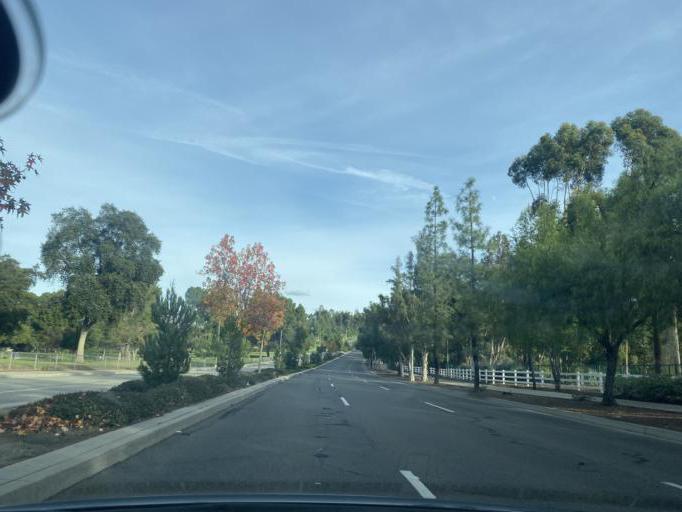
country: US
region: California
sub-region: Orange County
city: Brea
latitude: 33.8996
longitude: -117.9010
